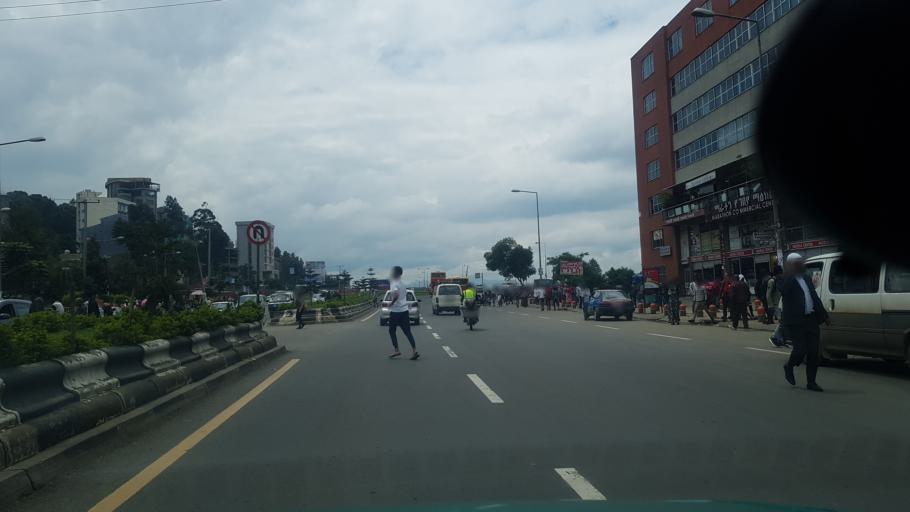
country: ET
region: Adis Abeba
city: Addis Ababa
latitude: 9.0222
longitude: 38.8000
